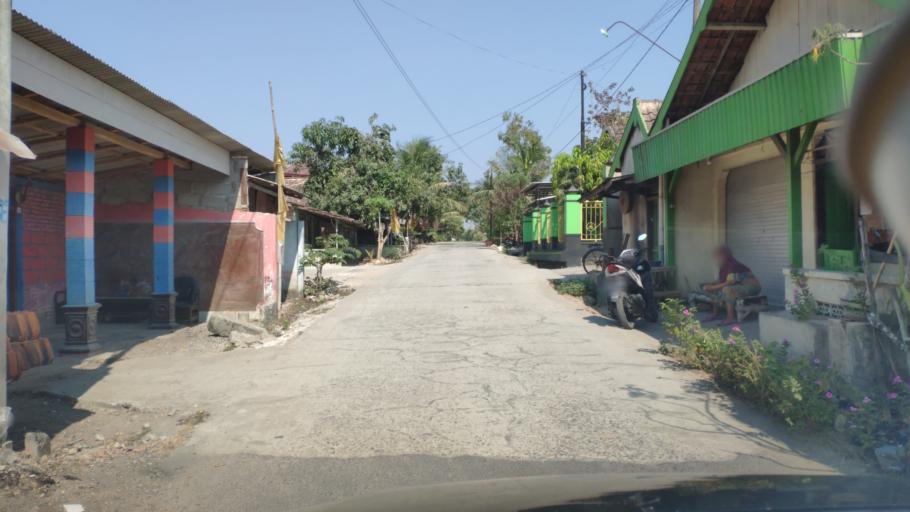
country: ID
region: Central Java
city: Medang
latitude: -6.9129
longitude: 111.4390
